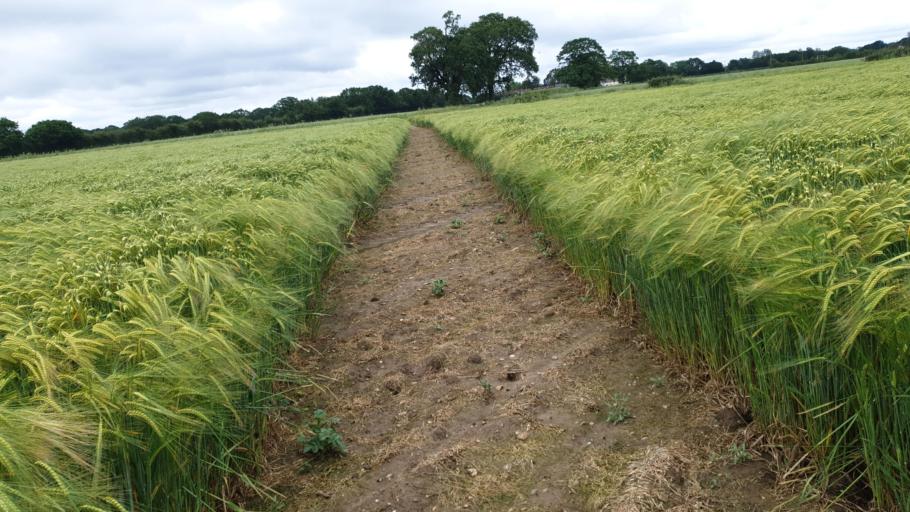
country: GB
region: England
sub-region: Essex
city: Great Bentley
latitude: 51.8787
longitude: 1.1124
